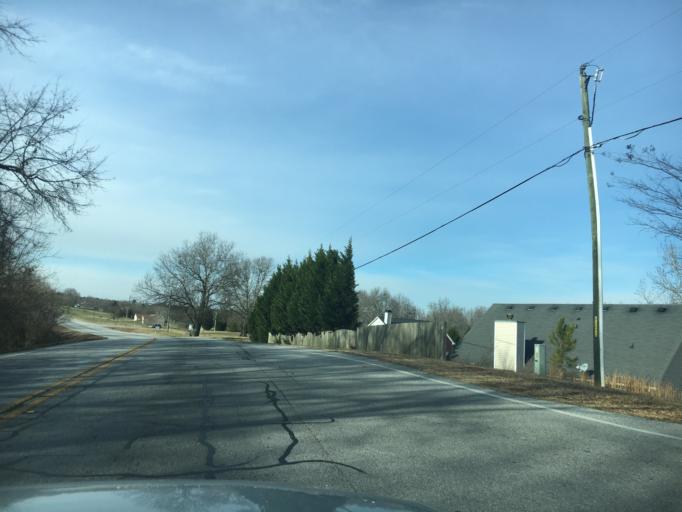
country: US
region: Georgia
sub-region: Jackson County
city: Hoschton
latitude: 34.0662
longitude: -83.7215
